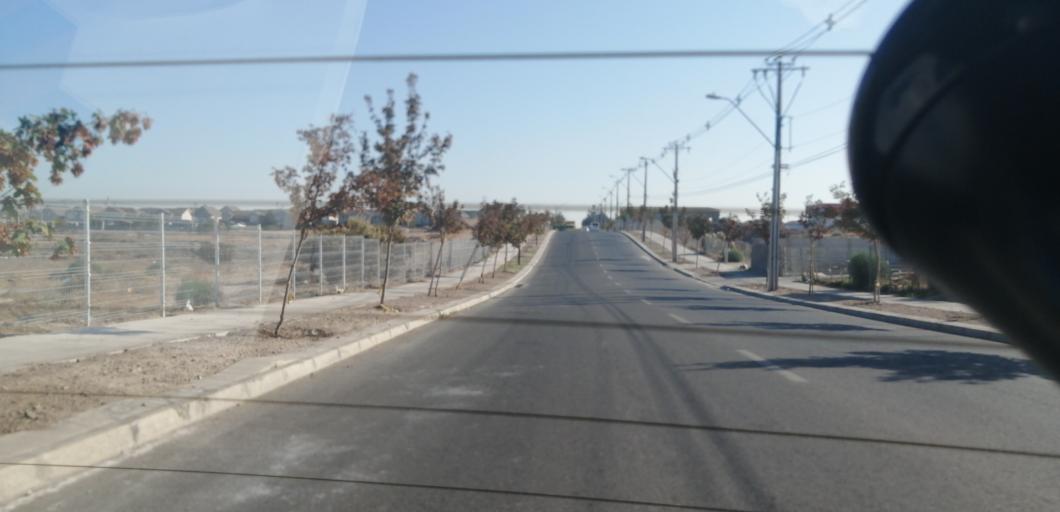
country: CL
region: Santiago Metropolitan
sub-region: Provincia de Santiago
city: Lo Prado
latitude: -33.4389
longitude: -70.7752
